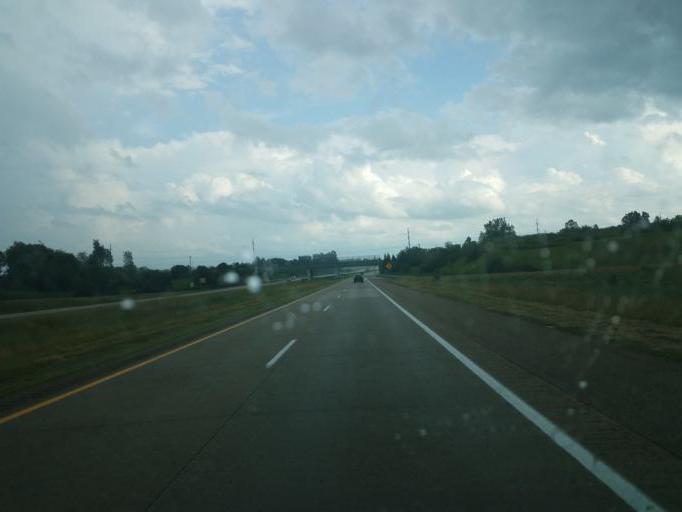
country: US
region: Michigan
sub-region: Calhoun County
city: Marshall
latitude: 42.2681
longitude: -84.9904
